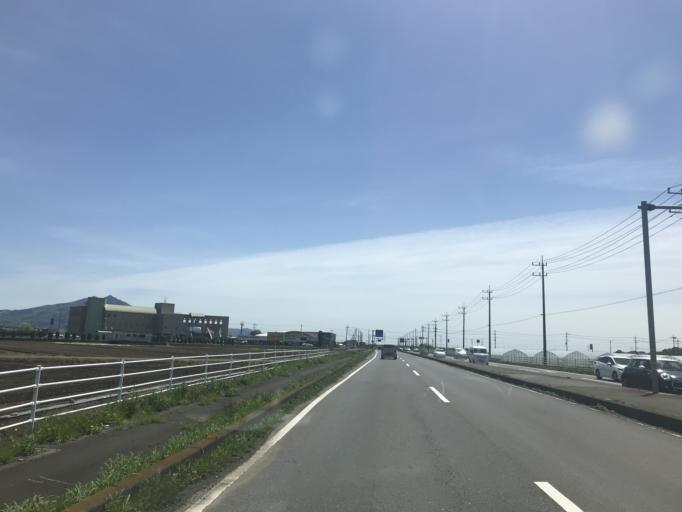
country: JP
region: Ibaraki
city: Shimodate
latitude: 36.2827
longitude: 139.9733
